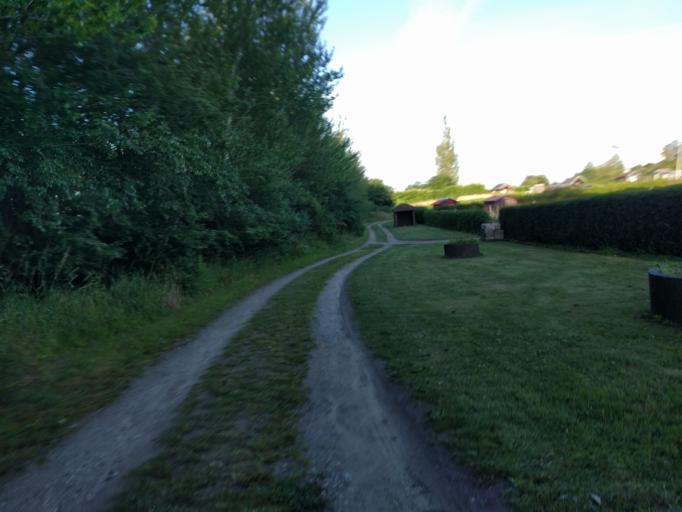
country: DK
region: South Denmark
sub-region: Kerteminde Kommune
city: Munkebo
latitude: 55.4647
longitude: 10.5512
